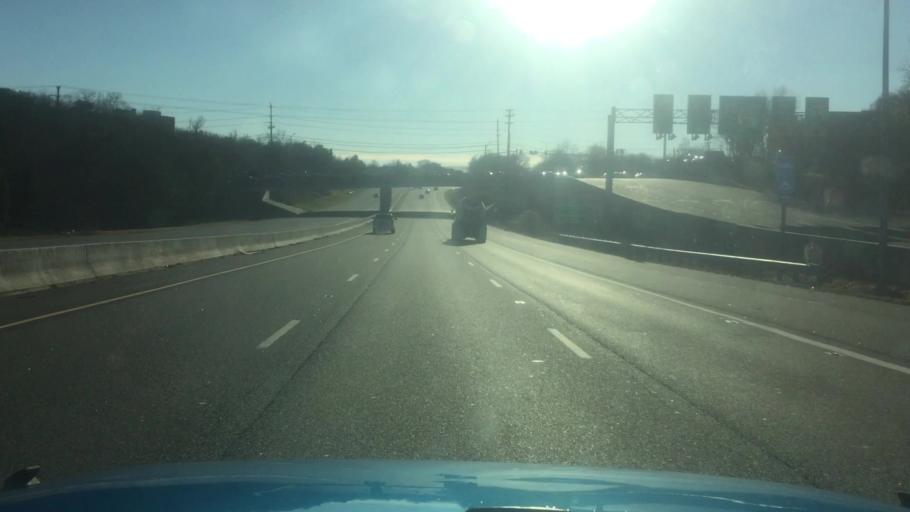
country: US
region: Maryland
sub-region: Prince George's County
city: Berwyn Heights
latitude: 38.9979
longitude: -76.8991
